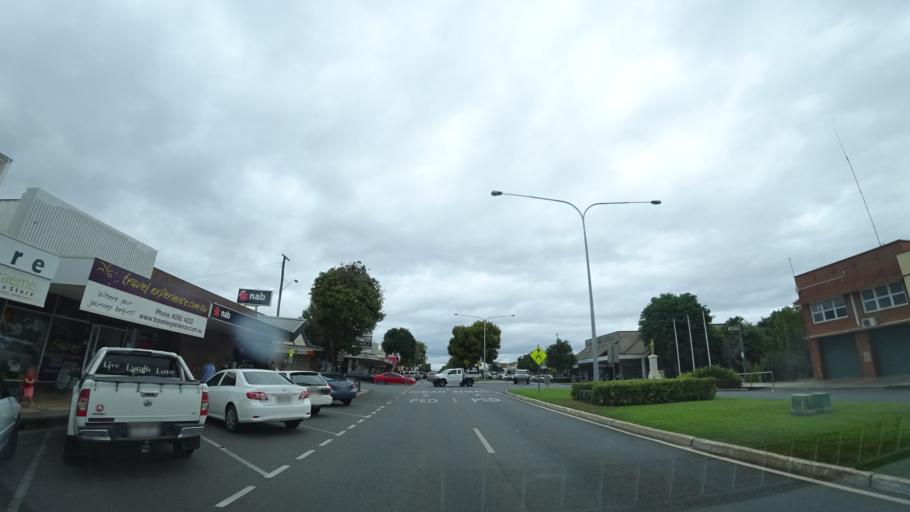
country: AU
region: Queensland
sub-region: Tablelands
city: Mareeba
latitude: -16.9928
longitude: 145.4224
